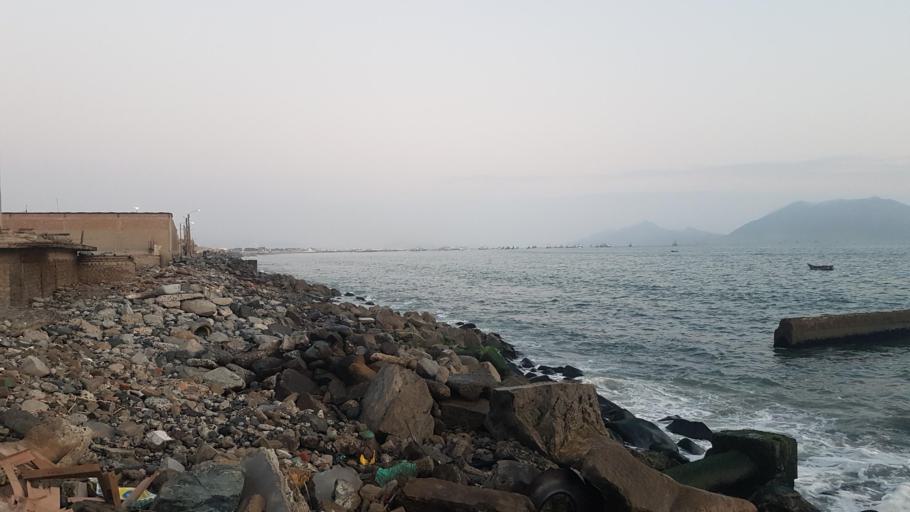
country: PE
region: Ancash
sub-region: Provincia de Santa
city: Chimbote
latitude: -9.0933
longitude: -78.5747
